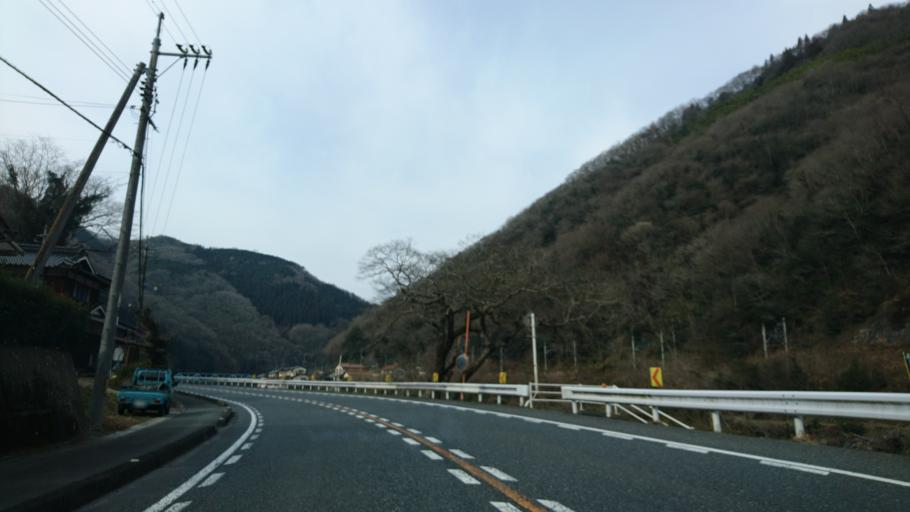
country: JP
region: Okayama
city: Takahashi
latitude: 34.8759
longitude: 133.5594
